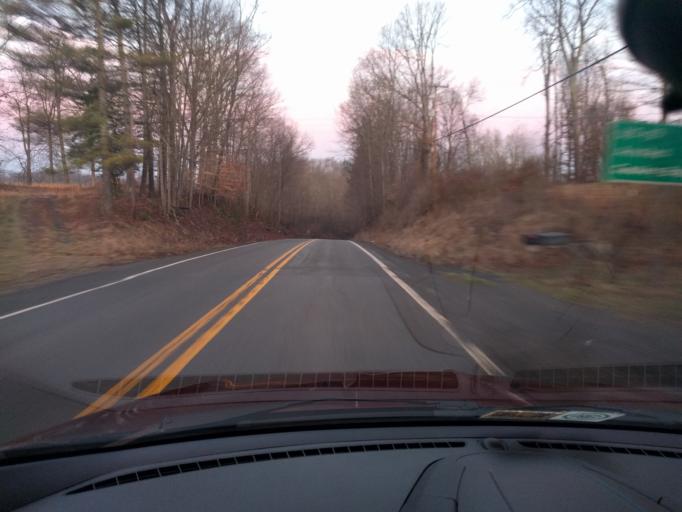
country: US
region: West Virginia
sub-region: Greenbrier County
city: Rainelle
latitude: 38.0218
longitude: -80.9148
